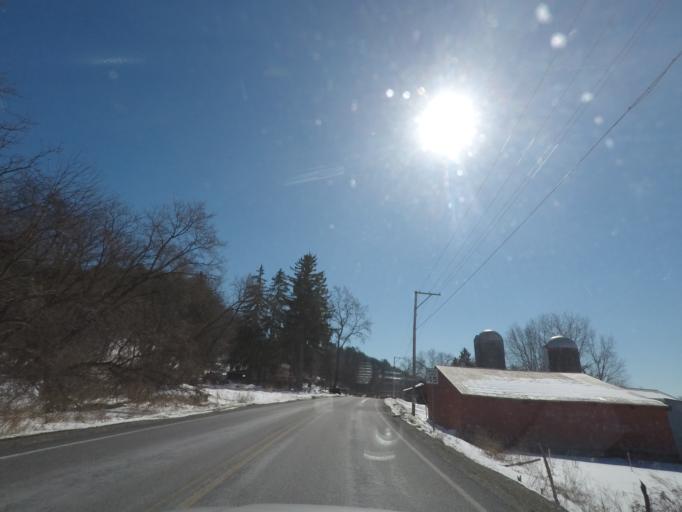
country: US
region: New York
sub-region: Saratoga County
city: Schuylerville
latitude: 43.1081
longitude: -73.5680
